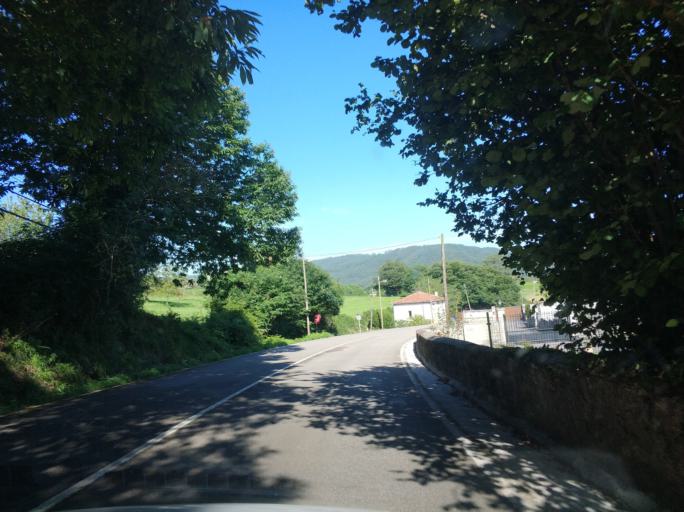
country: ES
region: Asturias
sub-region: Province of Asturias
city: Cudillero
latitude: 43.5468
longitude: -6.2199
